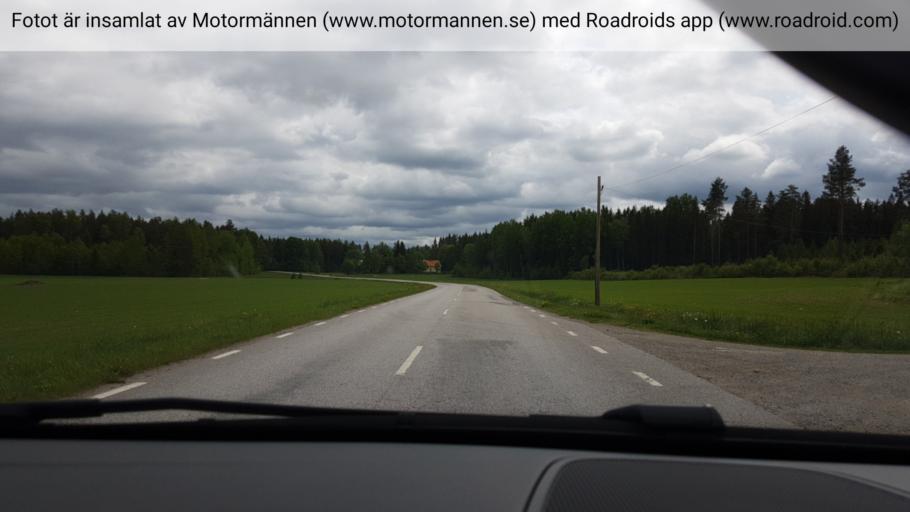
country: SE
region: Uppsala
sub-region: Heby Kommun
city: Tarnsjo
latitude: 60.1282
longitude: 16.9954
